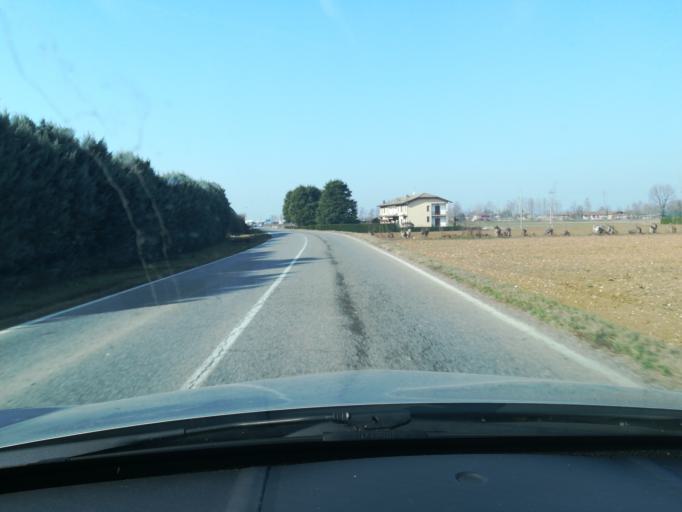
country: IT
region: Lombardy
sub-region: Provincia di Bergamo
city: Palosco
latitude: 45.5998
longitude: 9.8548
